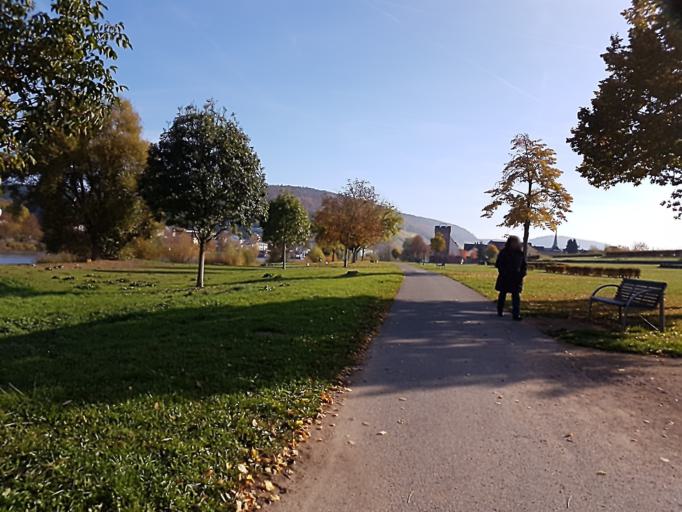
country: DE
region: Bavaria
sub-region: Regierungsbezirk Unterfranken
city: Worth am Main
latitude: 49.8002
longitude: 9.1532
